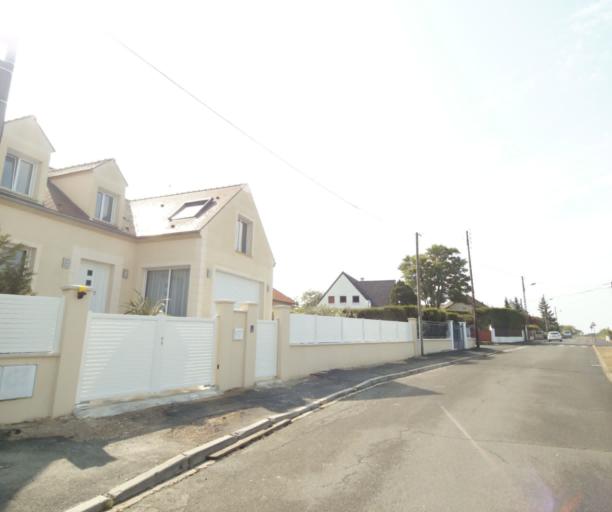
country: FR
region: Ile-de-France
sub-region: Departement des Yvelines
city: Maurecourt
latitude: 49.0012
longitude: 2.0736
